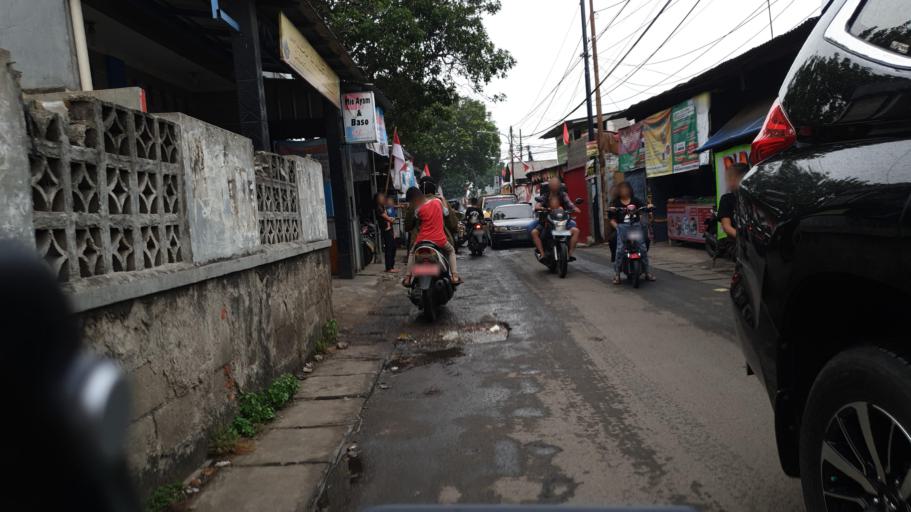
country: ID
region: West Java
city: Pamulang
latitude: -6.3311
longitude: 106.7698
